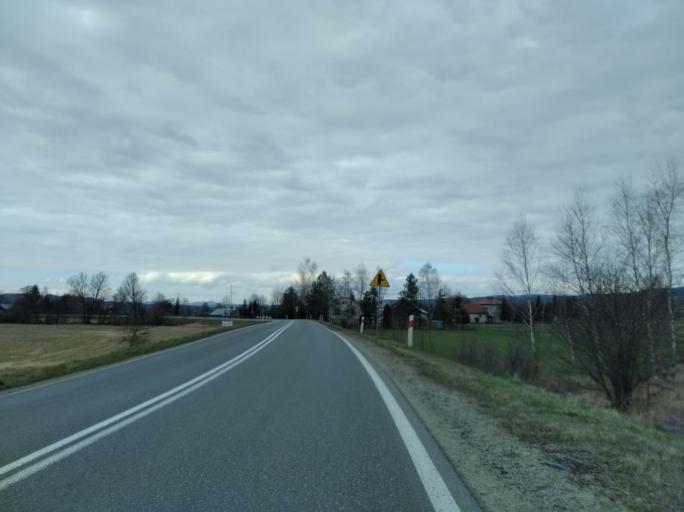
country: PL
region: Subcarpathian Voivodeship
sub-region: Powiat krosnienski
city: Wojaszowka
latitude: 49.7905
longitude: 21.6597
